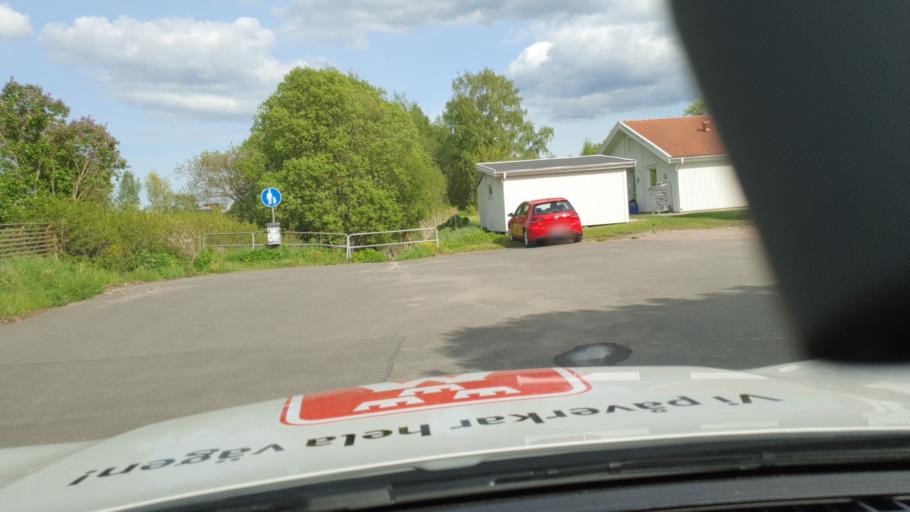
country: SE
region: Vaestra Goetaland
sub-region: Skovde Kommun
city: Skoevde
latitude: 58.3892
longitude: 13.8711
